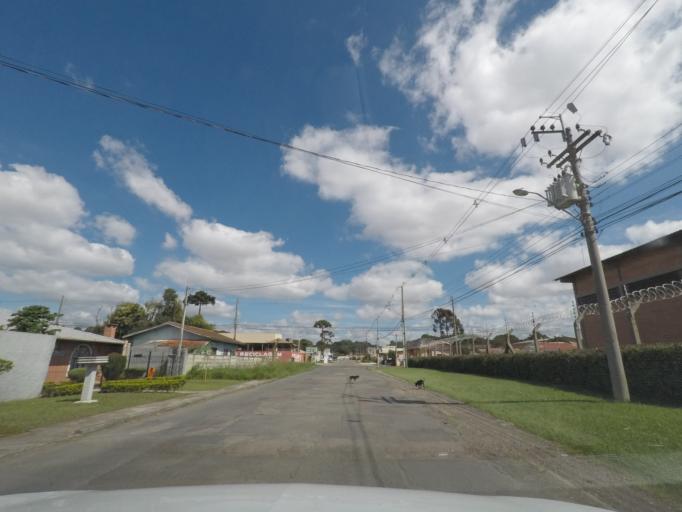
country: BR
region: Parana
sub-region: Sao Jose Dos Pinhais
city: Sao Jose dos Pinhais
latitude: -25.5038
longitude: -49.2332
